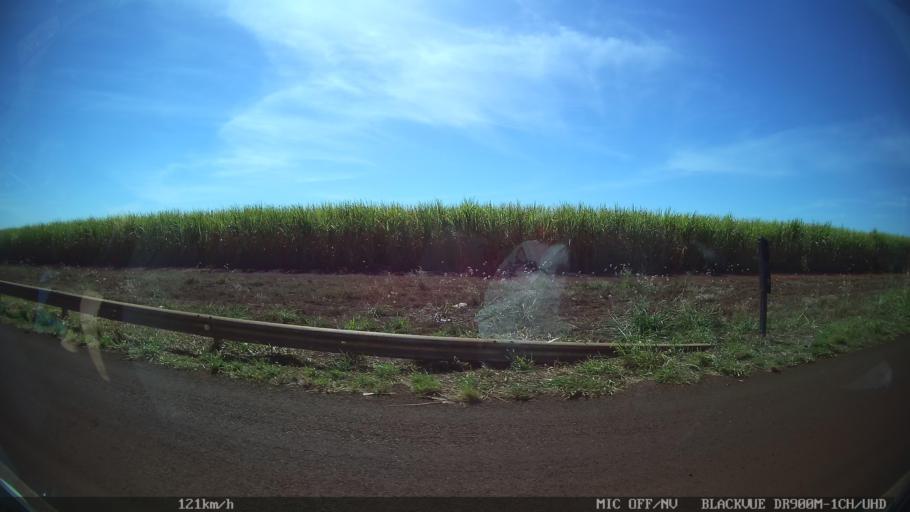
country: BR
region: Sao Paulo
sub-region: Guaira
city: Guaira
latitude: -20.4436
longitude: -48.3170
